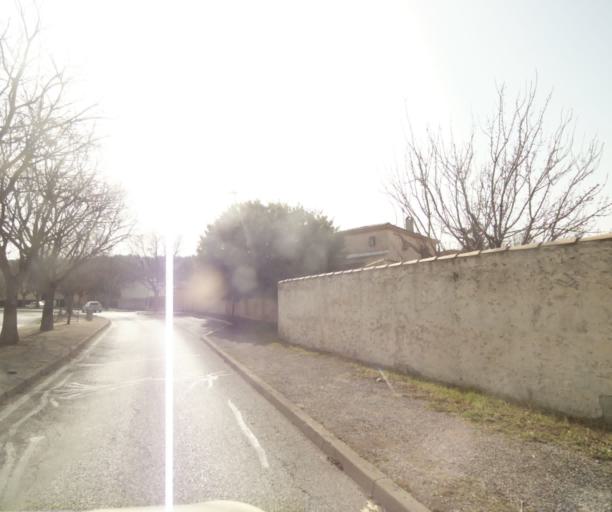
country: FR
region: Provence-Alpes-Cote d'Azur
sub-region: Departement des Bouches-du-Rhone
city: Gardanne
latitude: 43.4401
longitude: 5.4581
